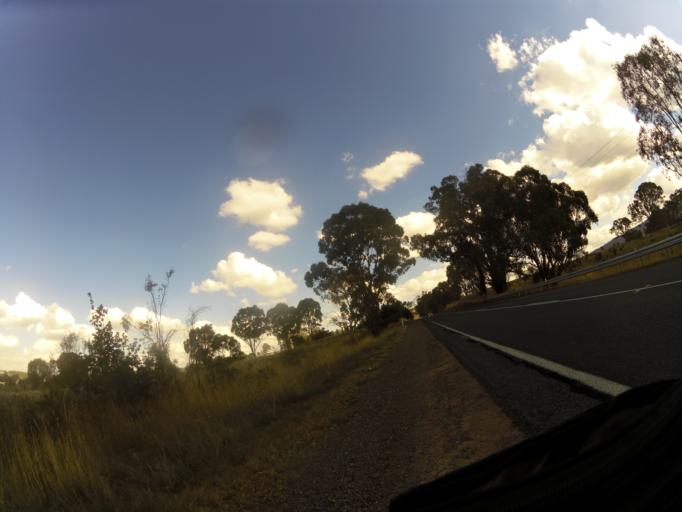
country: AU
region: Victoria
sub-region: Mansfield
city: Mansfield
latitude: -36.9358
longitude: 145.9995
